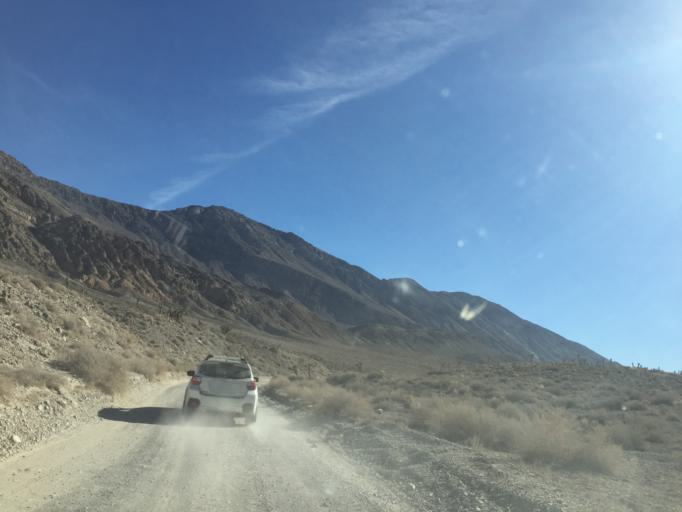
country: US
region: California
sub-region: Inyo County
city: Lone Pine
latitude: 36.8739
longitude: -117.5005
